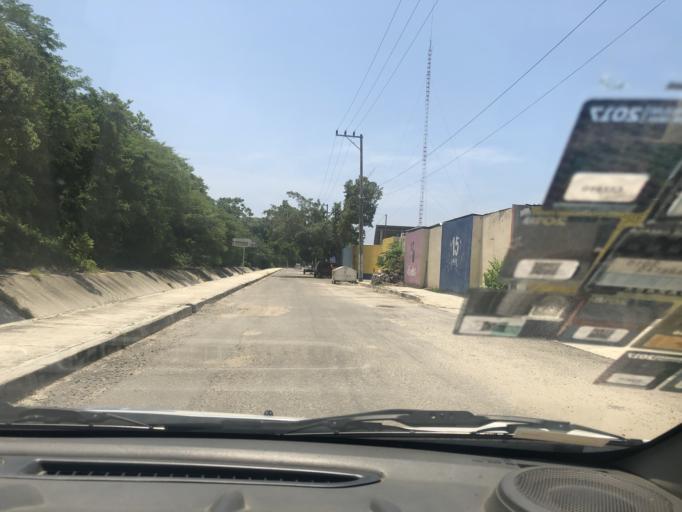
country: MX
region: Oaxaca
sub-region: Santa Maria Huatulco
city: Sector H Tres
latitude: 15.7779
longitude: -96.1502
